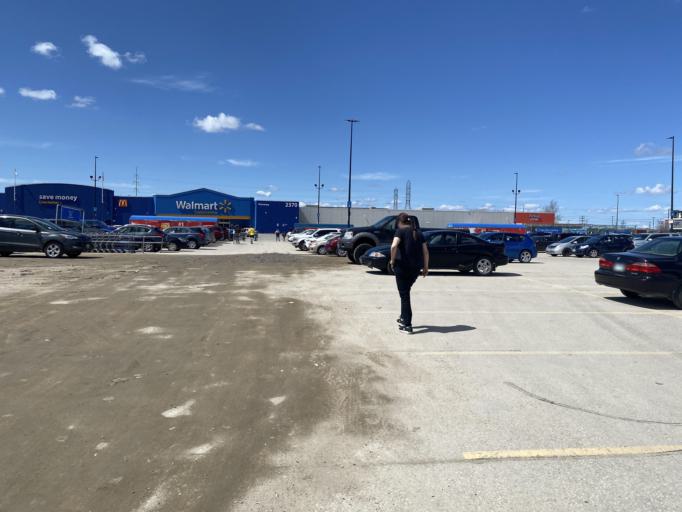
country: CA
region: Manitoba
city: Winnipeg
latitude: 49.9572
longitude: -97.1479
